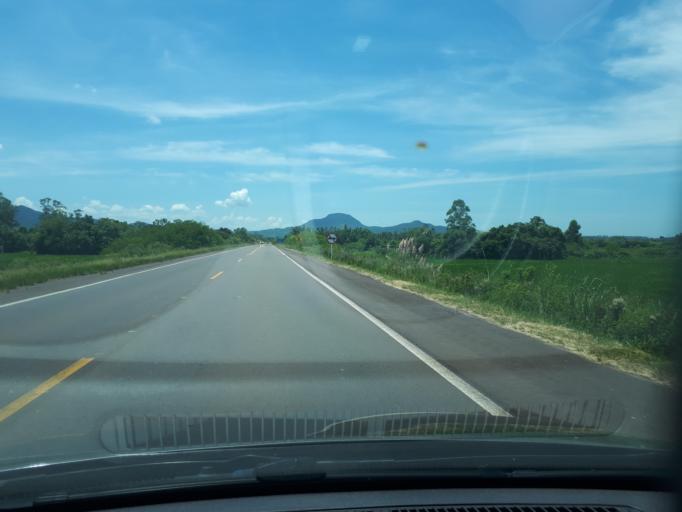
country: BR
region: Rio Grande do Sul
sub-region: Candelaria
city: Candelaria
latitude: -29.7281
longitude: -52.9374
